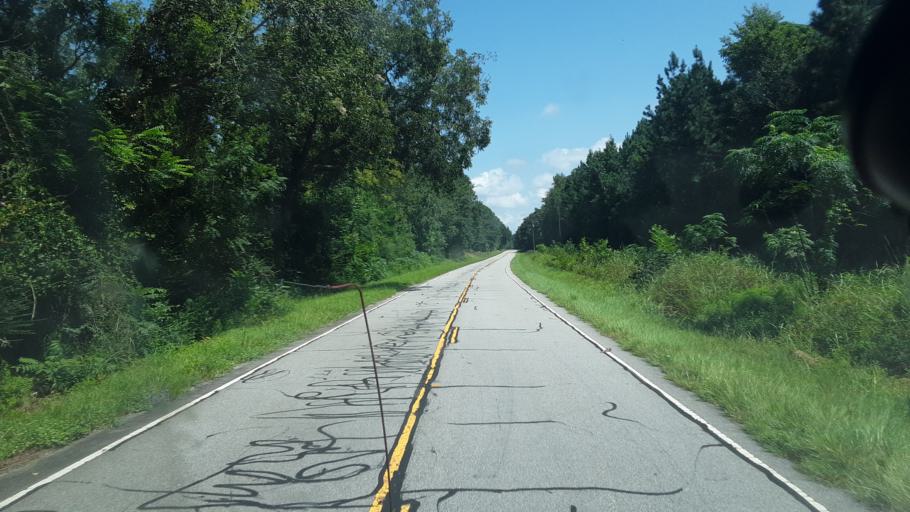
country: US
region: South Carolina
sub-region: Orangeburg County
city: Edisto
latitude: 33.5950
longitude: -81.0280
